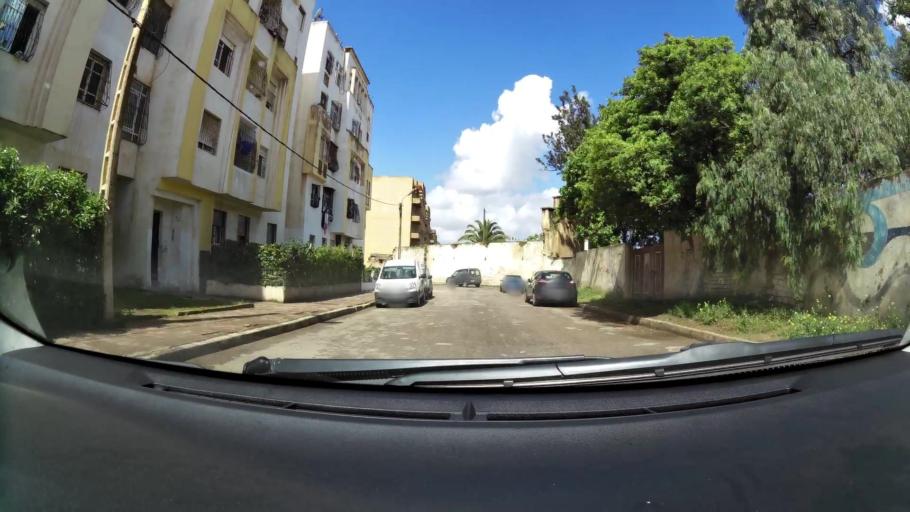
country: MA
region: Grand Casablanca
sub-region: Mediouna
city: Tit Mellil
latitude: 33.5539
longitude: -7.4789
